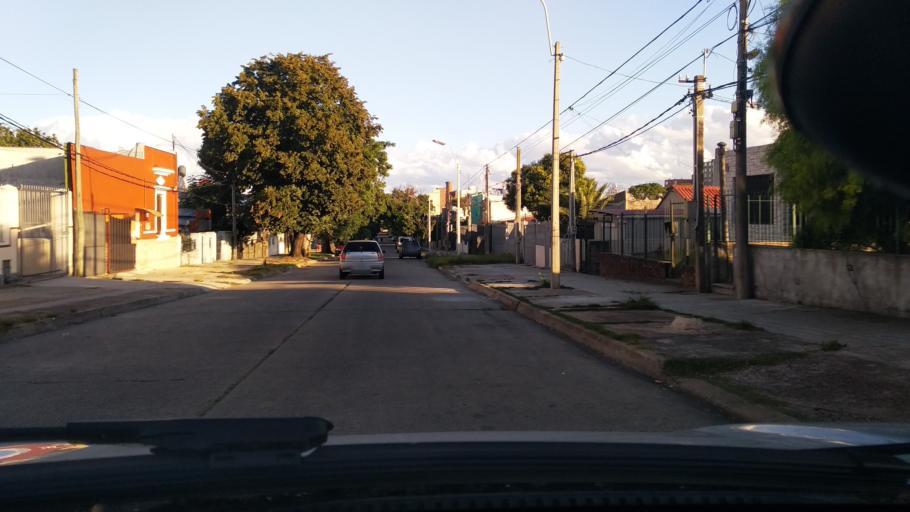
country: UY
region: Montevideo
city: Montevideo
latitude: -34.8795
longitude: -56.1434
